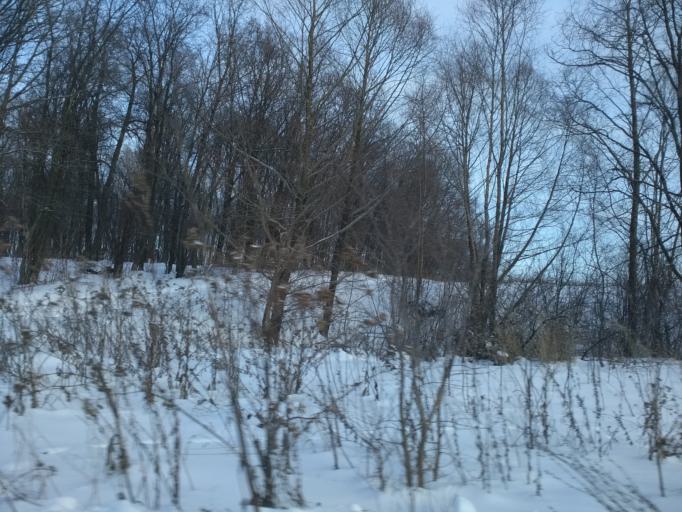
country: RU
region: Bashkortostan
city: Iglino
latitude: 54.7731
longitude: 56.5464
